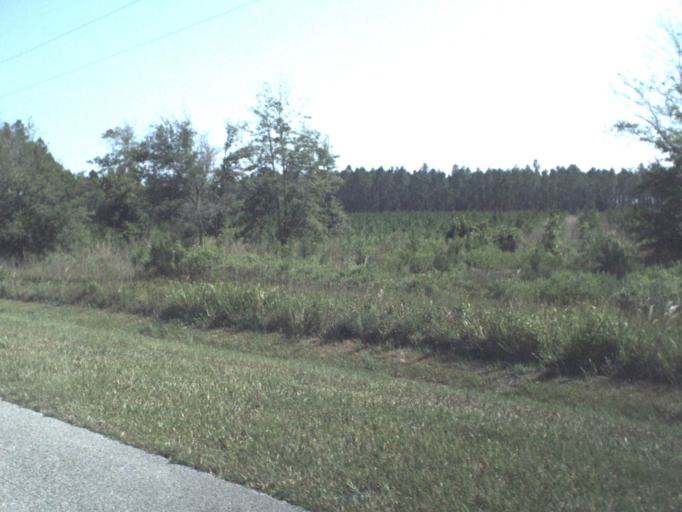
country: US
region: Florida
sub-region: Alachua County
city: Waldo
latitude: 29.7031
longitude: -82.1338
